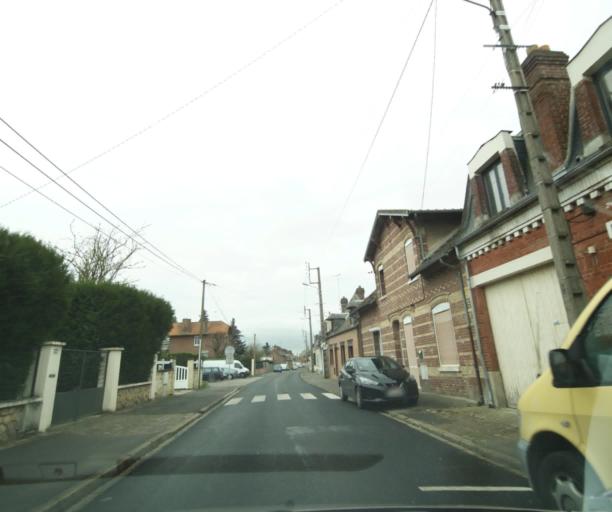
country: FR
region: Picardie
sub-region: Departement de l'Oise
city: Noyon
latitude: 49.5870
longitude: 3.0096
